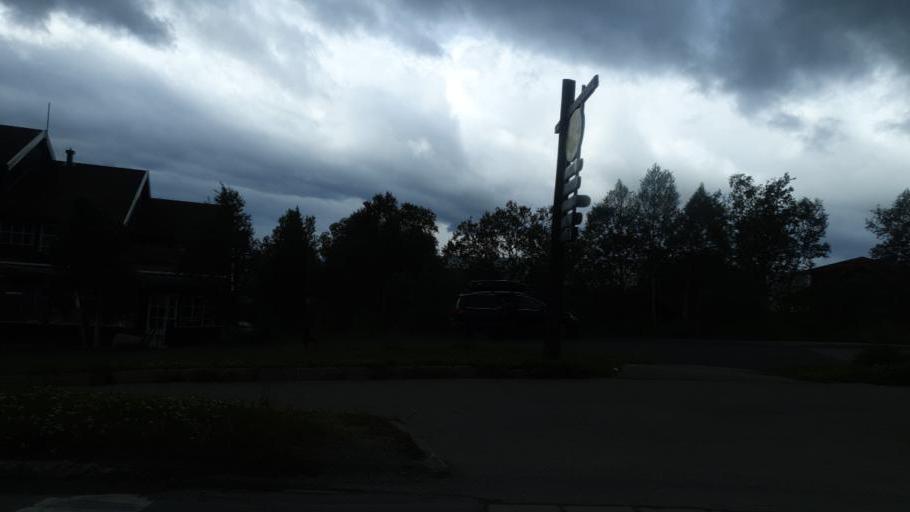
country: NO
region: Oppland
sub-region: Vestre Slidre
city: Slidre
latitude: 61.2486
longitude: 8.9065
